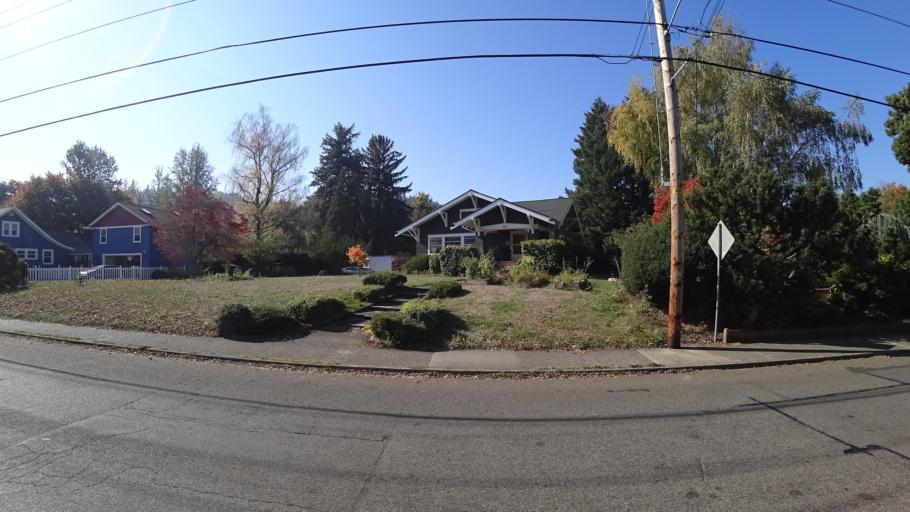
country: US
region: Oregon
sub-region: Multnomah County
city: Gresham
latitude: 45.4941
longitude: -122.4269
